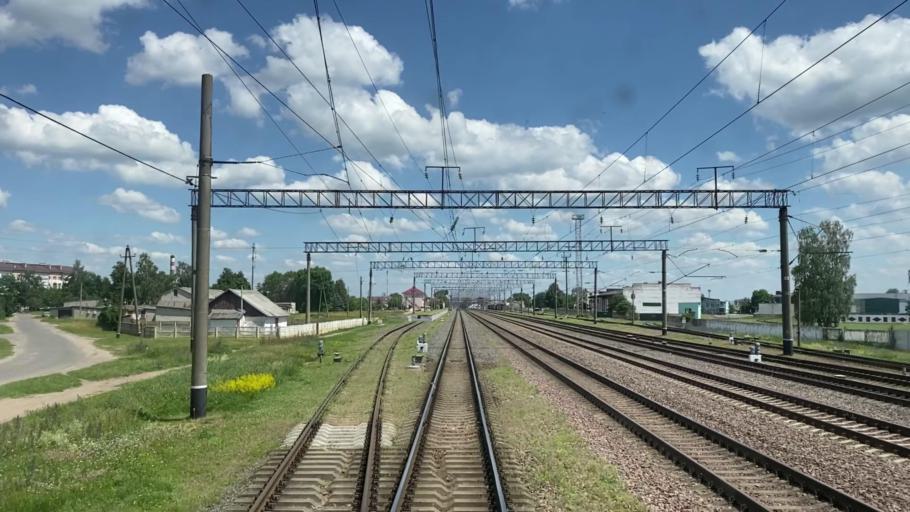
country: BY
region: Brest
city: Ivatsevichy
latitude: 52.7055
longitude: 25.3365
